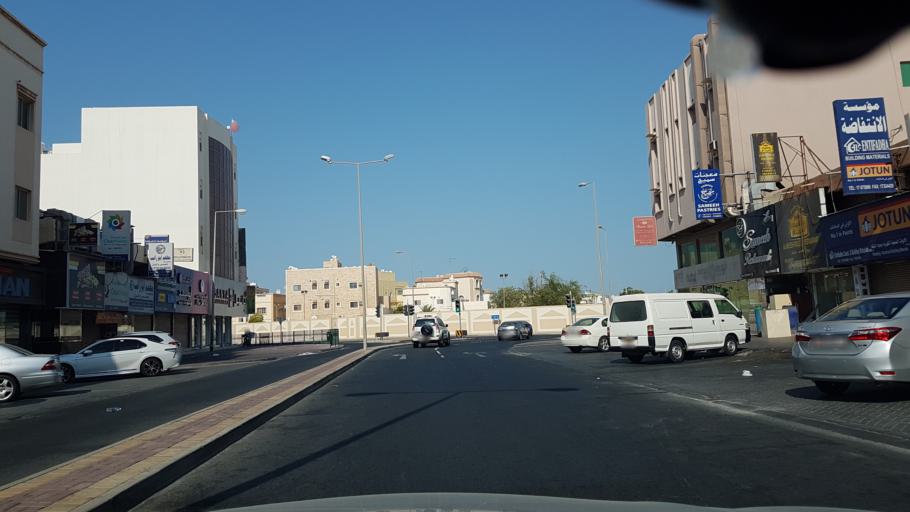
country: BH
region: Muharraq
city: Al Hadd
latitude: 26.2564
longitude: 50.6358
